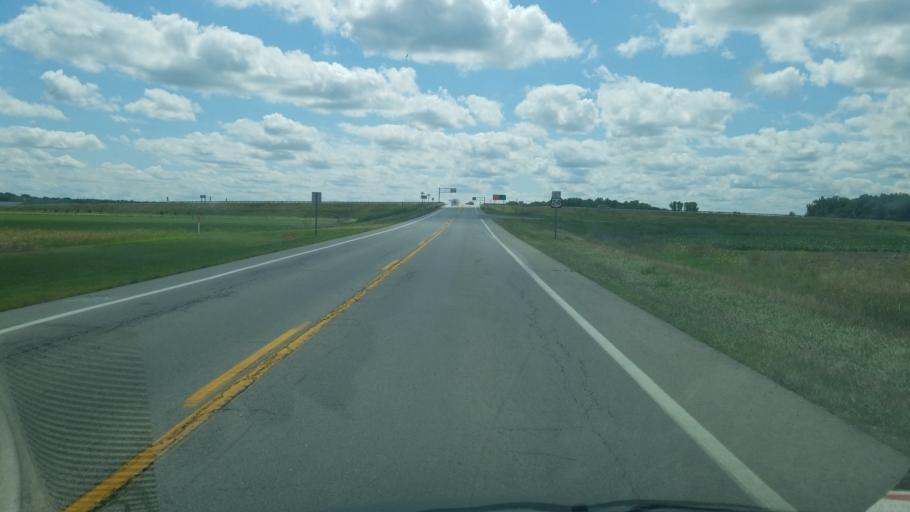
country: US
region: Ohio
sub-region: Henry County
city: Liberty Center
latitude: 41.4324
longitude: -84.0087
